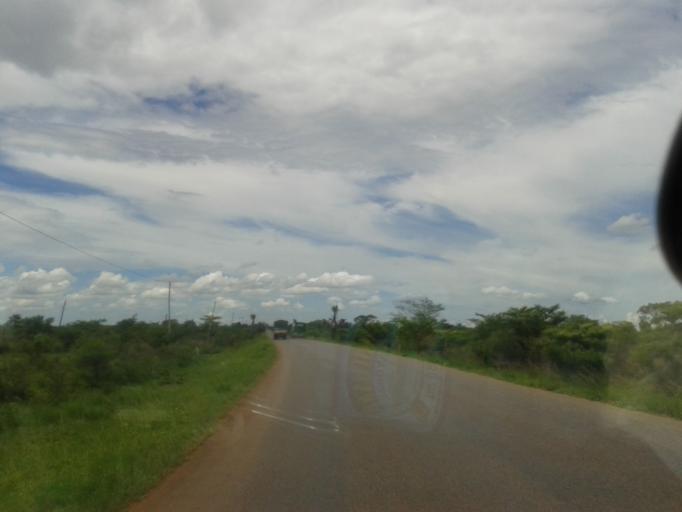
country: UG
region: Western Region
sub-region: Kiryandongo District
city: Masindi Port
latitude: 1.5209
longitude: 32.0482
